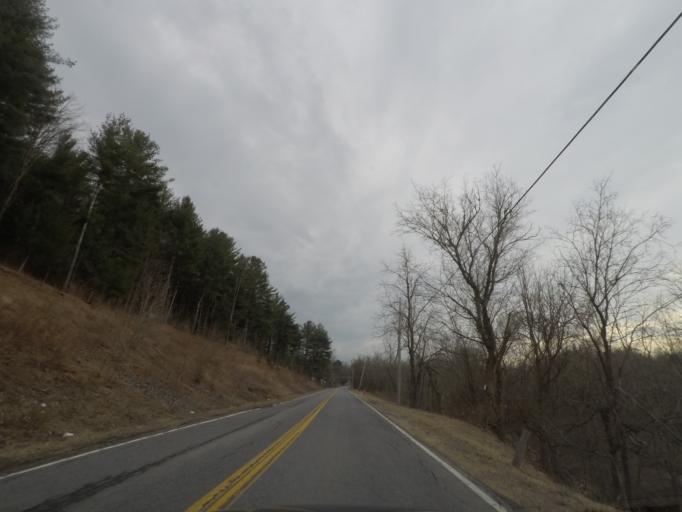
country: US
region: New York
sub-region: Washington County
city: Greenwich
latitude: 43.0678
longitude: -73.4992
